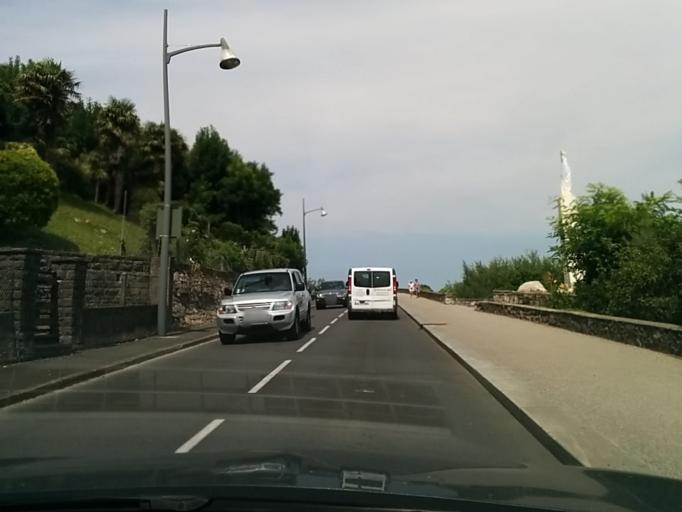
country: FR
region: Aquitaine
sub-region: Departement des Pyrenees-Atlantiques
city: Ciboure
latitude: 43.3882
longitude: -1.6713
